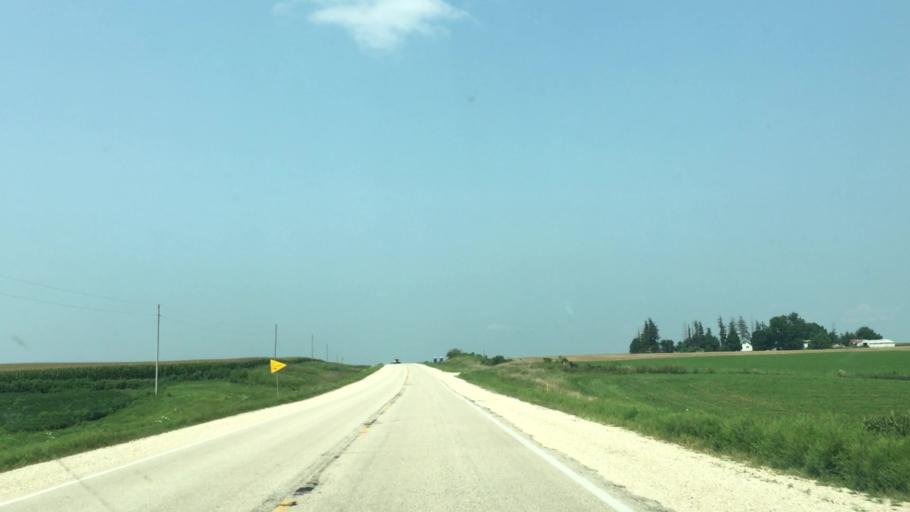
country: US
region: Iowa
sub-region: Fayette County
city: West Union
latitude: 42.9927
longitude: -91.8239
